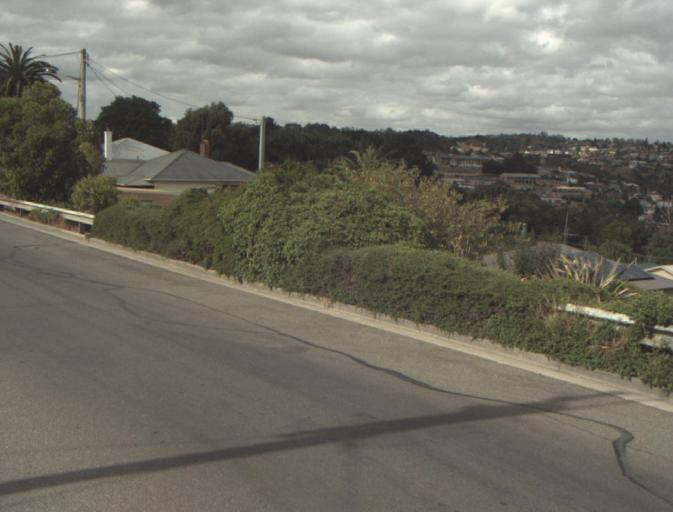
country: AU
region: Tasmania
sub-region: Launceston
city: East Launceston
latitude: -41.4531
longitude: 147.1543
